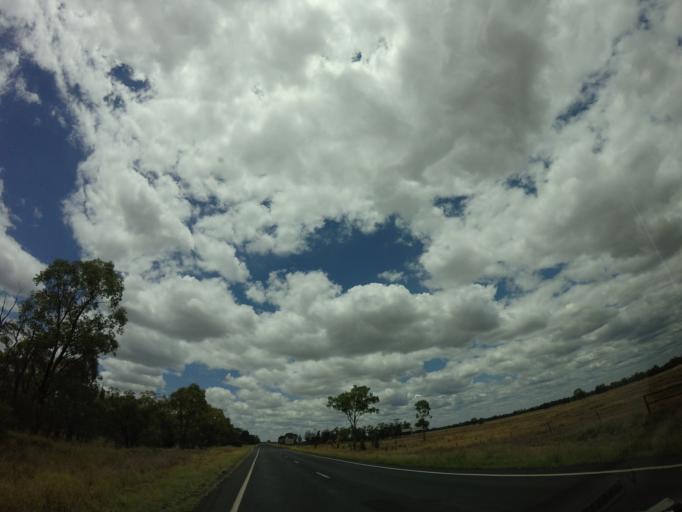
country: AU
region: Queensland
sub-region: Goondiwindi
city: Goondiwindi
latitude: -28.1581
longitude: 150.6612
